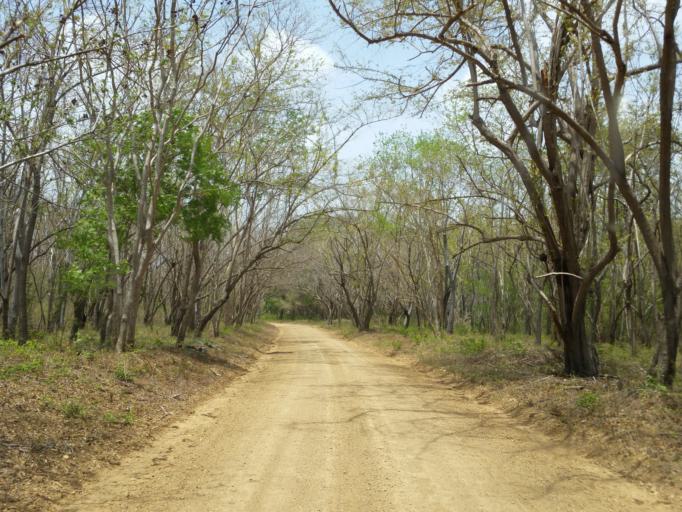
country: NI
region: Rivas
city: Tola
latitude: 11.4190
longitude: -86.0603
